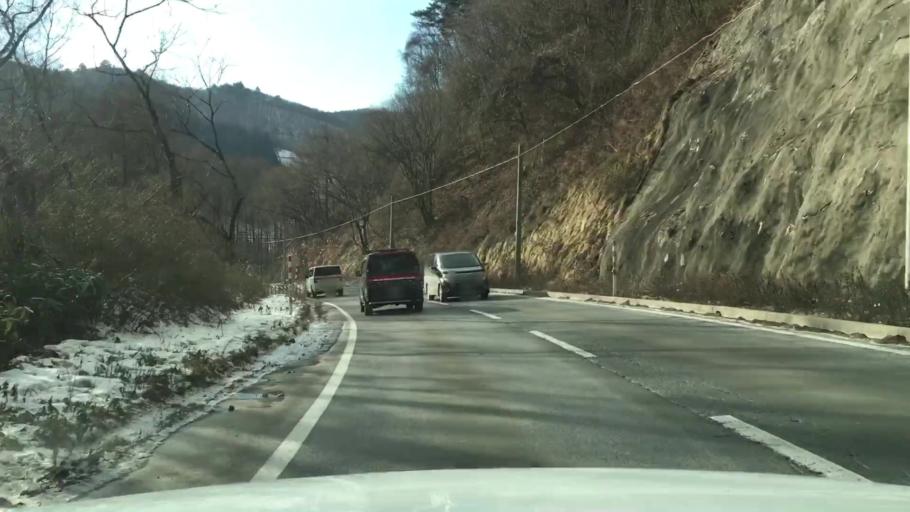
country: JP
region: Iwate
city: Morioka-shi
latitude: 39.6658
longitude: 141.3073
